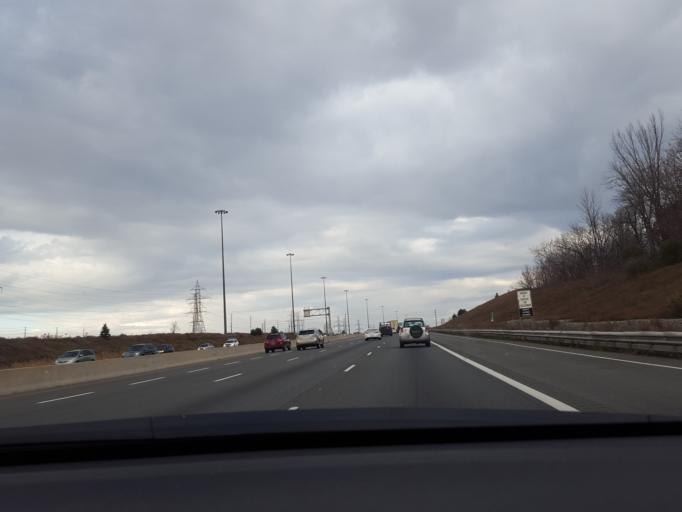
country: CA
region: Ontario
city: Mississauga
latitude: 43.5721
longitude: -79.6736
